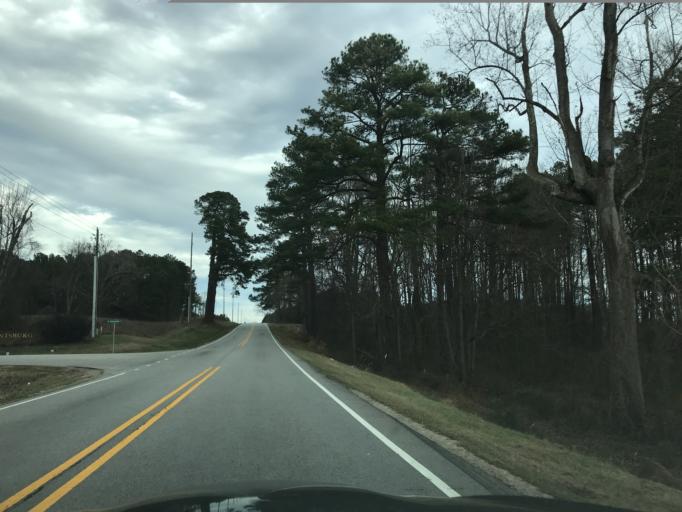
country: US
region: North Carolina
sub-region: Franklin County
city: Louisburg
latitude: 36.0364
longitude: -78.3510
